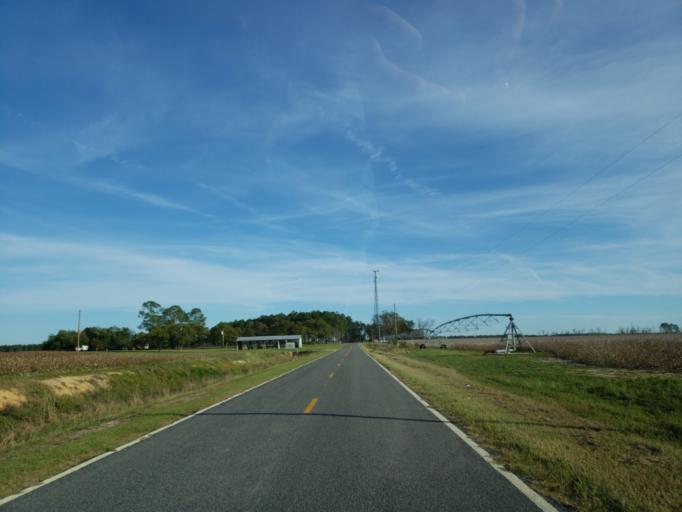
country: US
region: Georgia
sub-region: Dooly County
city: Vienna
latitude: 32.0750
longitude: -83.7841
